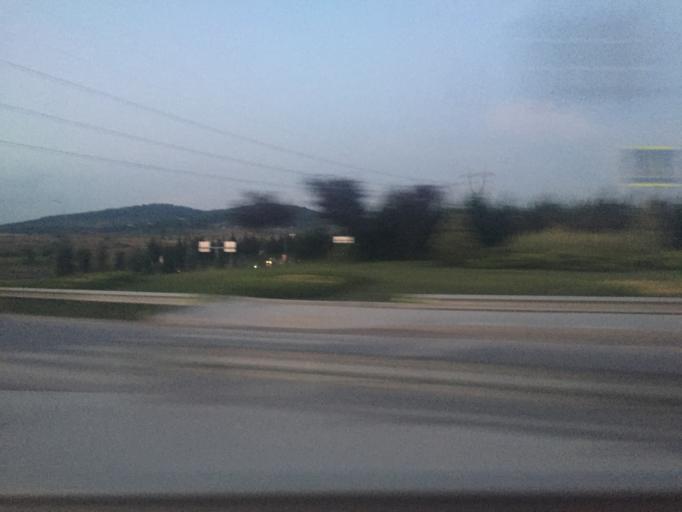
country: TR
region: Istanbul
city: Pendik
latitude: 40.9138
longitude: 29.3129
